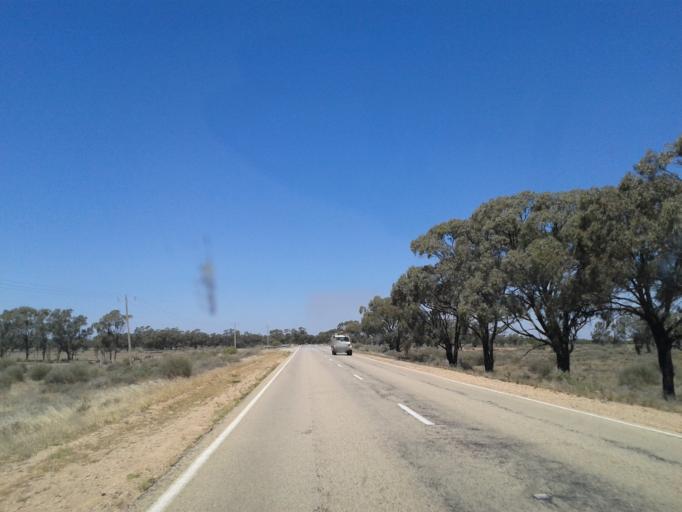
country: AU
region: Victoria
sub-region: Swan Hill
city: Swan Hill
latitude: -34.7718
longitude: 143.2402
